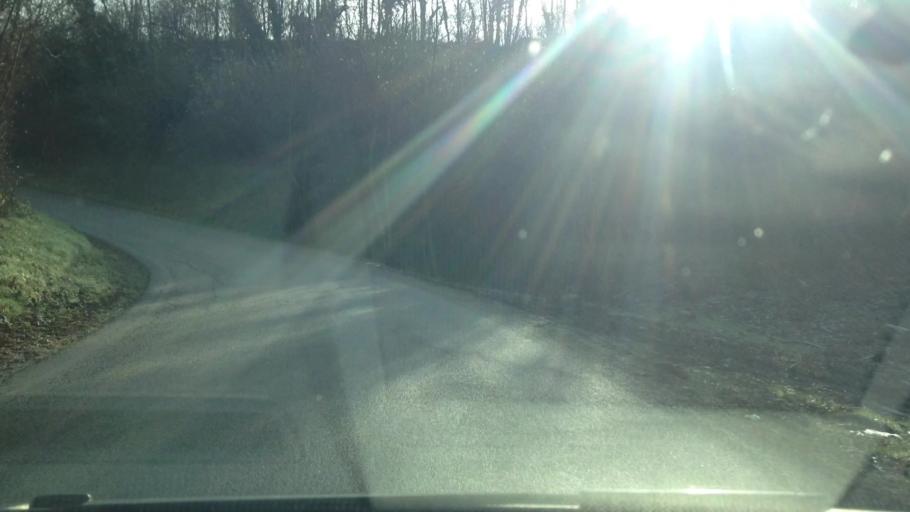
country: IT
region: Piedmont
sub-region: Provincia di Alessandria
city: Masio
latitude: 44.8548
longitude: 8.4148
